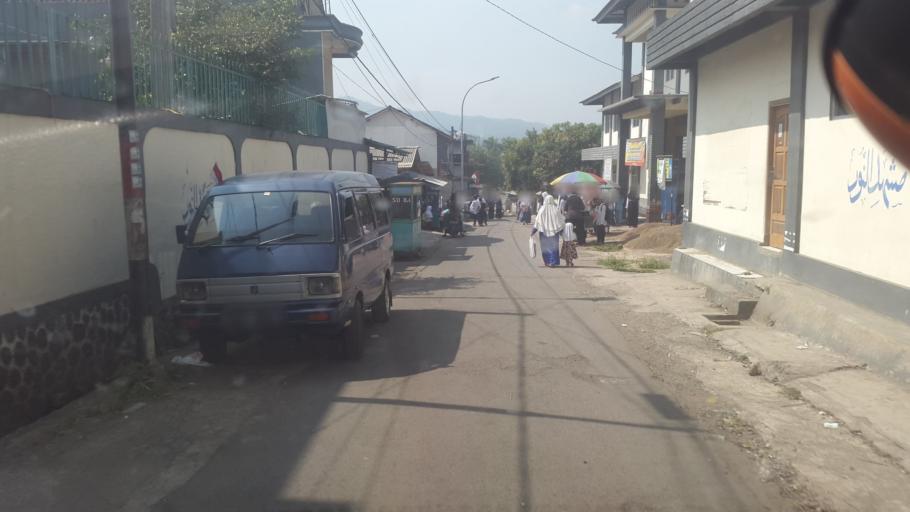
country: ID
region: West Java
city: Pasirreungit
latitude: -6.9292
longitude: 107.0122
